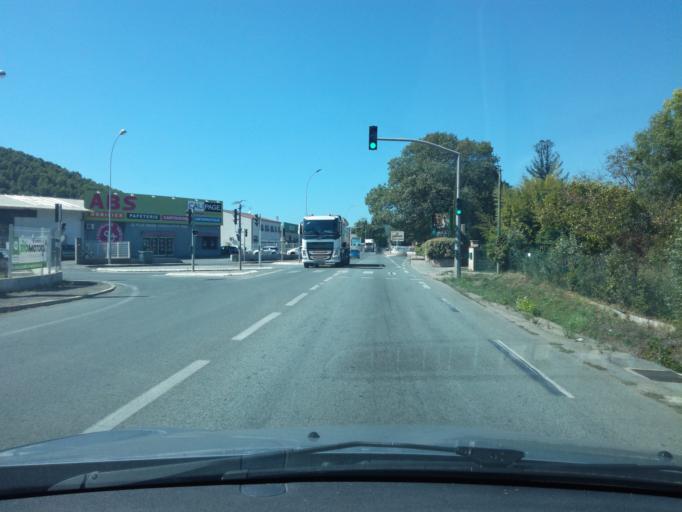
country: FR
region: Provence-Alpes-Cote d'Azur
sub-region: Departement du Var
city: Draguignan
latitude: 43.5220
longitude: 6.4661
